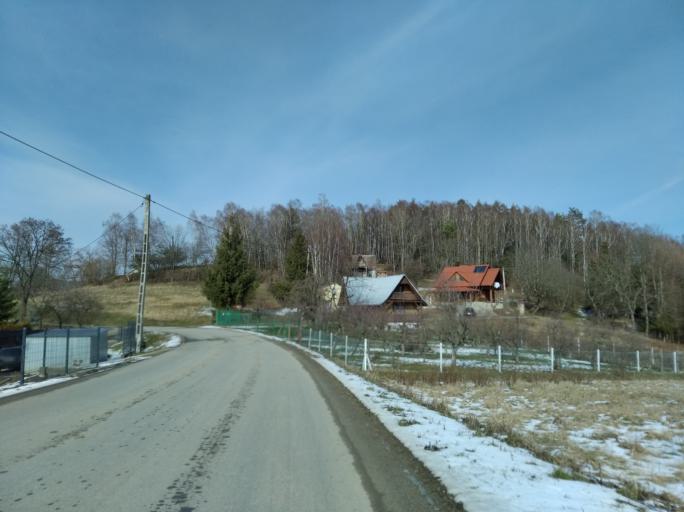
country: PL
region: Subcarpathian Voivodeship
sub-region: Powiat krosnienski
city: Korczyna
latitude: 49.7380
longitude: 21.7859
